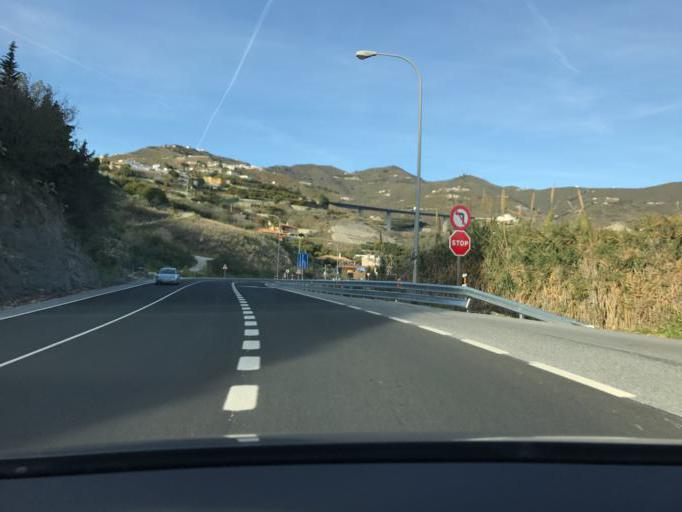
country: ES
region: Andalusia
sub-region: Provincia de Granada
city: Almunecar
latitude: 36.7504
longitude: -3.6583
